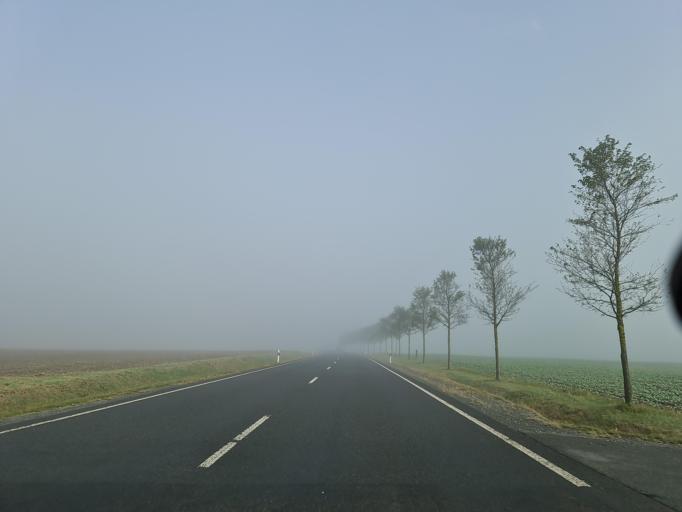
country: DE
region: Thuringia
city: Dittersdorf
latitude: 50.6346
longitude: 11.8152
